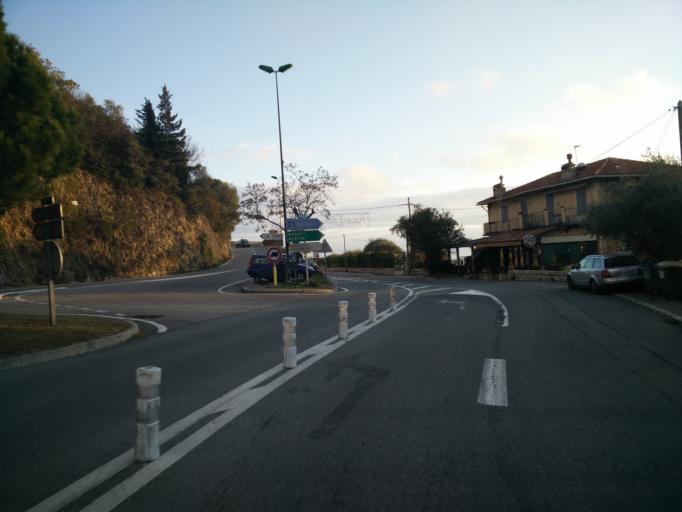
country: FR
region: Provence-Alpes-Cote d'Azur
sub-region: Departement des Alpes-Maritimes
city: Eze
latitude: 43.7300
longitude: 7.3664
